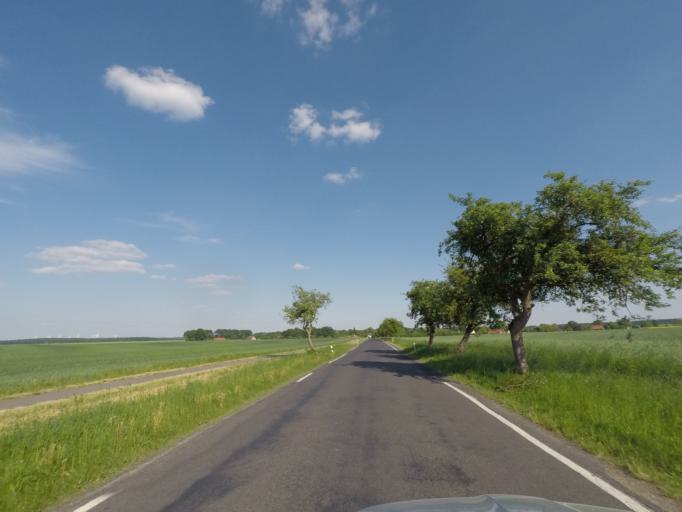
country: DE
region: Brandenburg
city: Werftpfuhl
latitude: 52.7326
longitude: 13.8606
